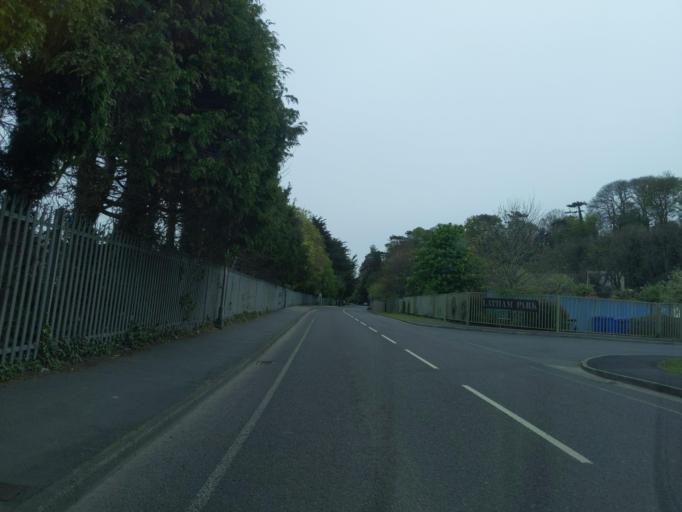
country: GB
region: England
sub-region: Cornwall
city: Par
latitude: 50.3560
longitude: -4.7119
